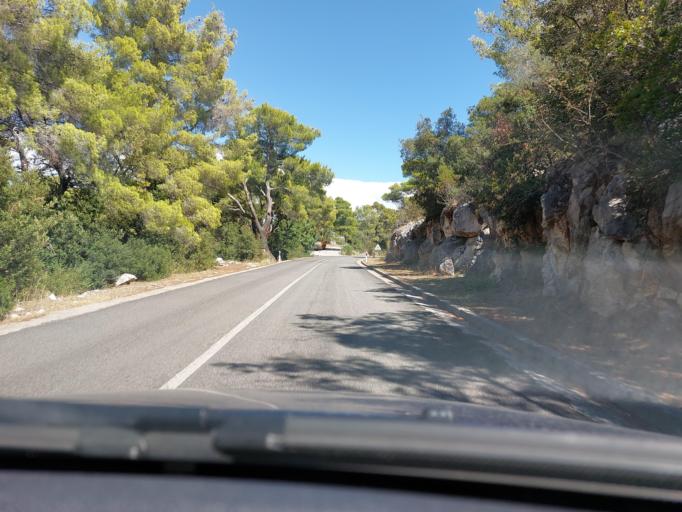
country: HR
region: Dubrovacko-Neretvanska
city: Smokvica
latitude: 42.7667
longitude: 16.8890
